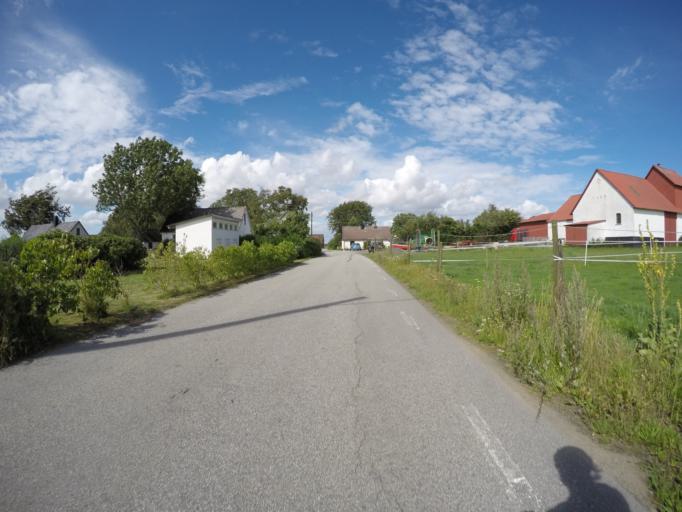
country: SE
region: Skane
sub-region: Simrishamns Kommun
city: Simrishamn
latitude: 55.4971
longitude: 14.2031
